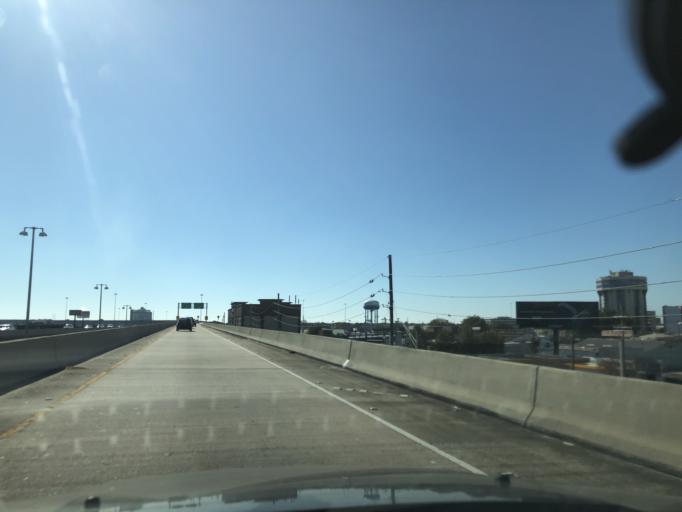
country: US
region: Louisiana
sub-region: Jefferson Parish
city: Metairie
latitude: 30.0036
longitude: -90.1554
